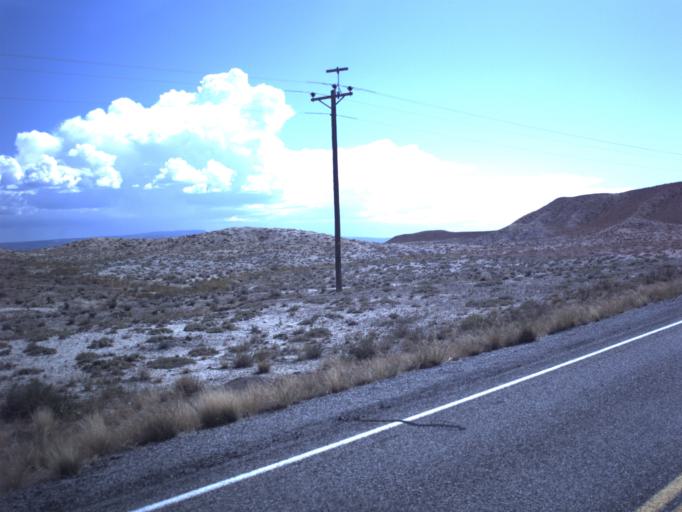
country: US
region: Utah
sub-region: Grand County
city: Moab
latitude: 38.9352
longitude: -109.3461
